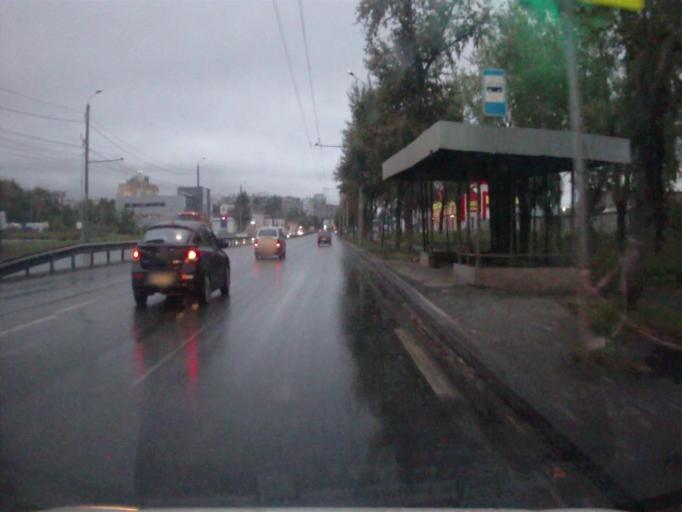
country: RU
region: Chelyabinsk
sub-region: Gorod Chelyabinsk
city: Chelyabinsk
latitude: 55.1370
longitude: 61.4613
